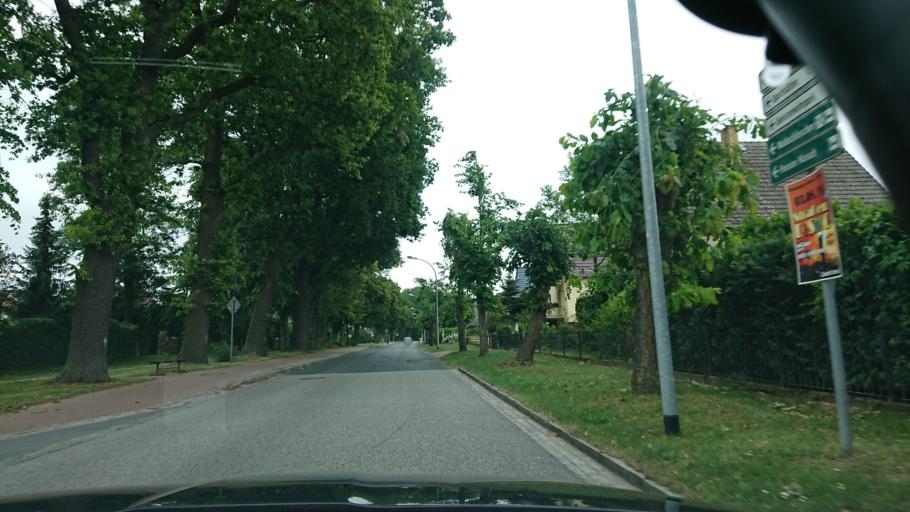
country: DE
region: Brandenburg
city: Kyritz
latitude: 52.9402
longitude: 12.4106
